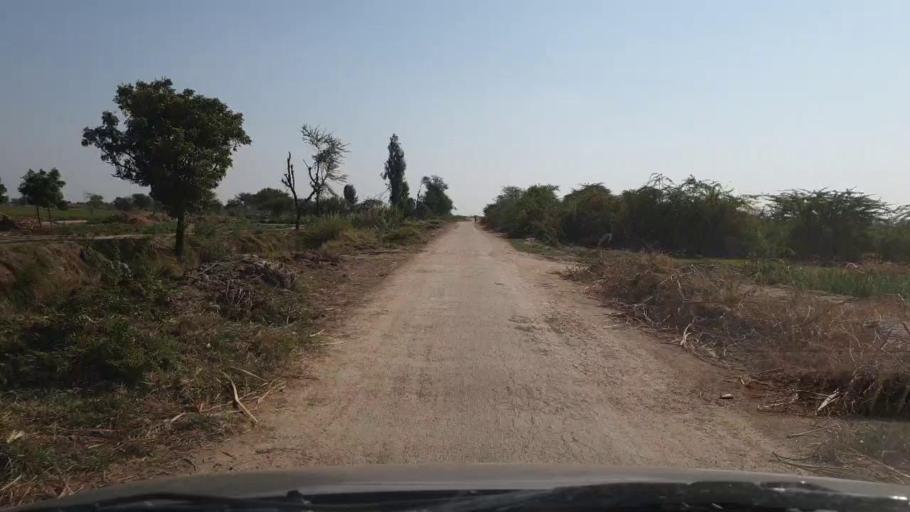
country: PK
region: Sindh
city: Samaro
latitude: 25.2106
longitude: 69.2748
